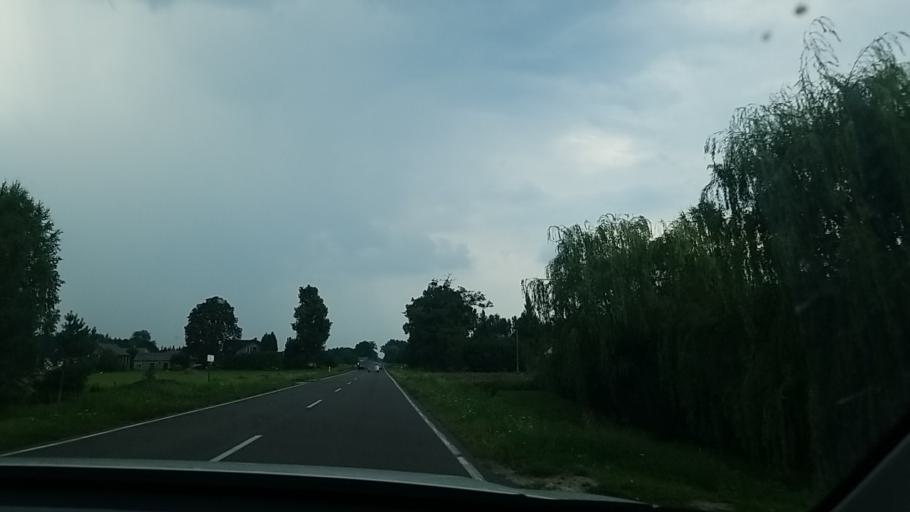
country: PL
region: Lublin Voivodeship
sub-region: Powiat leczynski
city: Cycow
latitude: 51.2584
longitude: 23.0933
